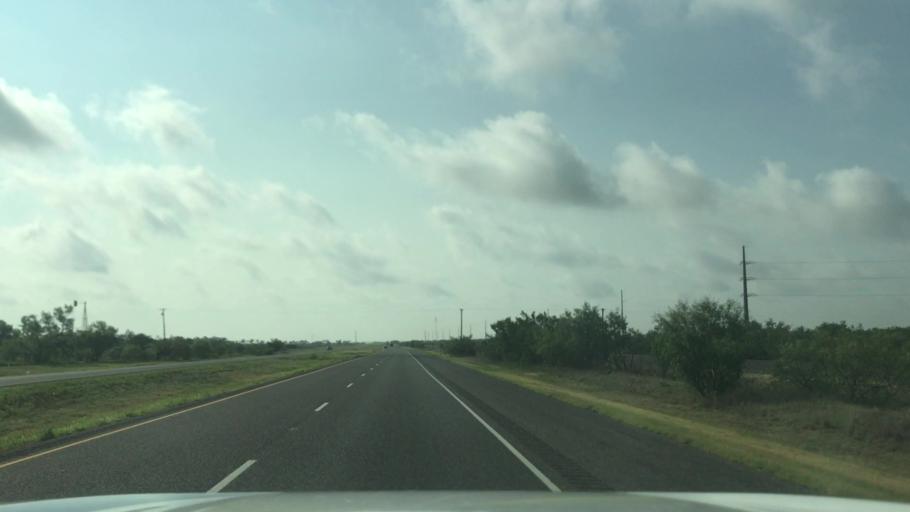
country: US
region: Texas
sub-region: Scurry County
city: Snyder
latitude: 32.8755
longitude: -101.0453
